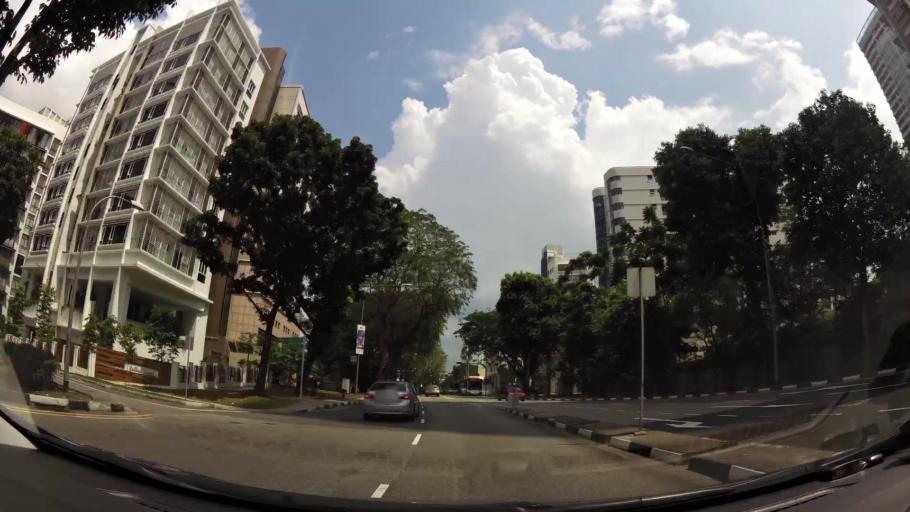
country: SG
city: Singapore
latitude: 1.2957
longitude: 103.8379
